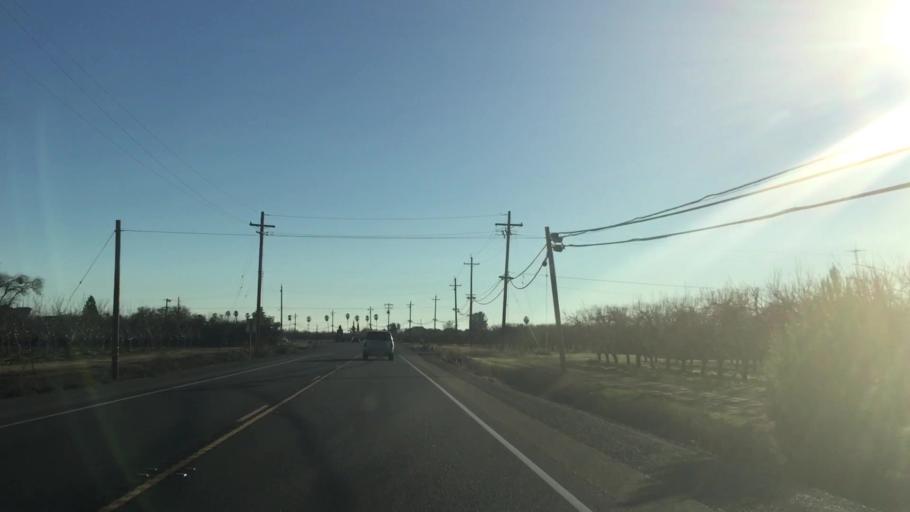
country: US
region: California
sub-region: Yuba County
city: Marysville
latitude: 39.2217
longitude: -121.6013
